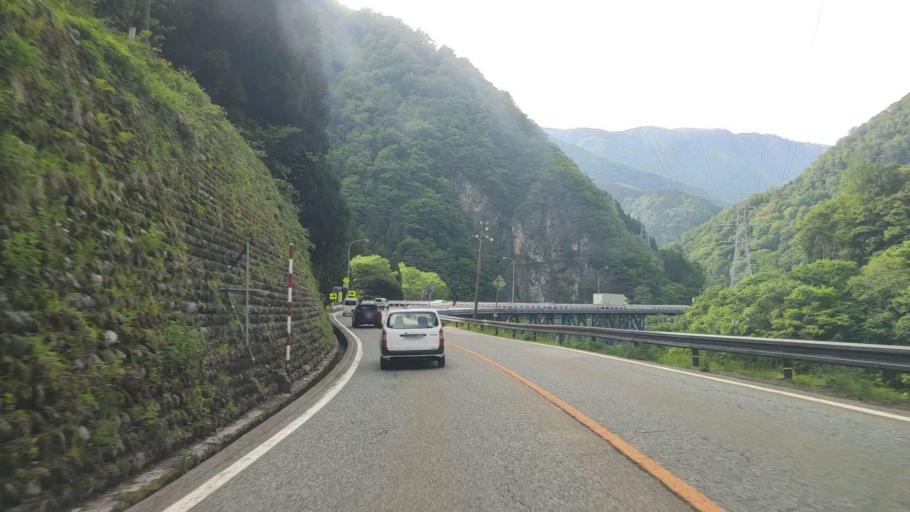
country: JP
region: Gifu
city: Takayama
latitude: 36.3674
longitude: 137.2840
